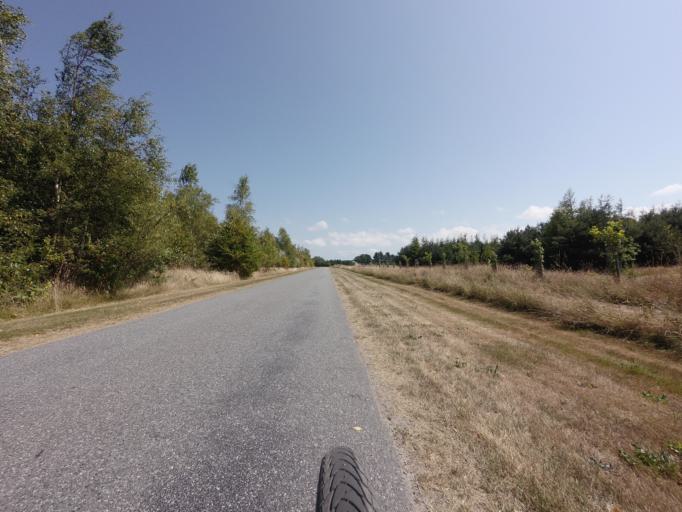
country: DK
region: North Denmark
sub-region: Laeso Kommune
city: Byrum
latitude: 57.2531
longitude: 10.9514
